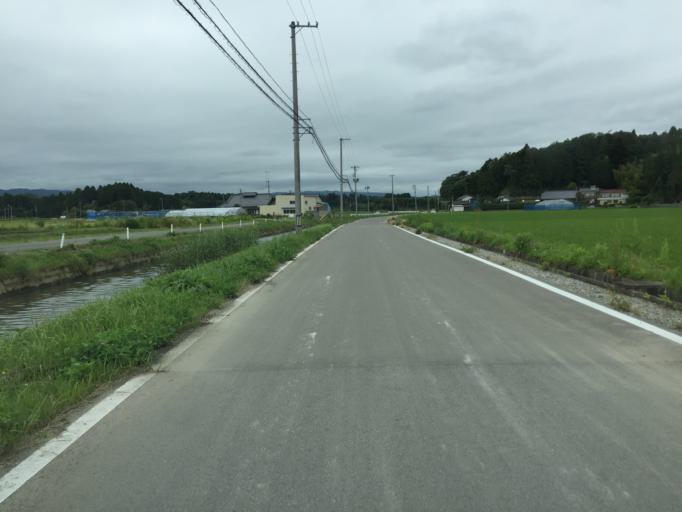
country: JP
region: Fukushima
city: Namie
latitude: 37.7370
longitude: 140.9769
